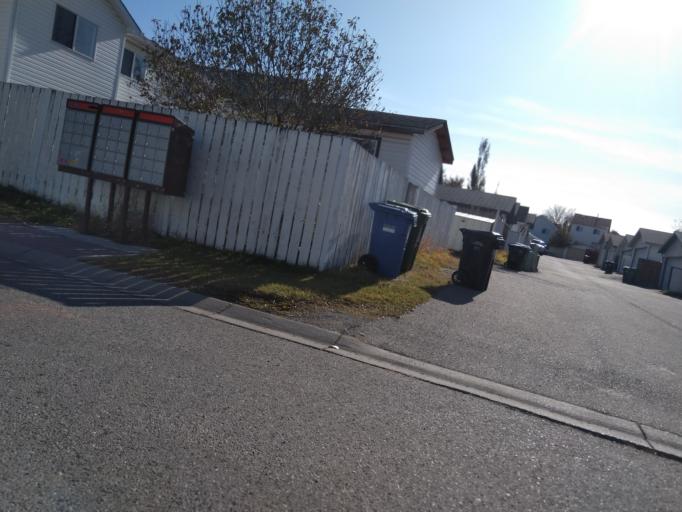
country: CA
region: Alberta
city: Calgary
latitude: 51.1537
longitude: -114.1095
